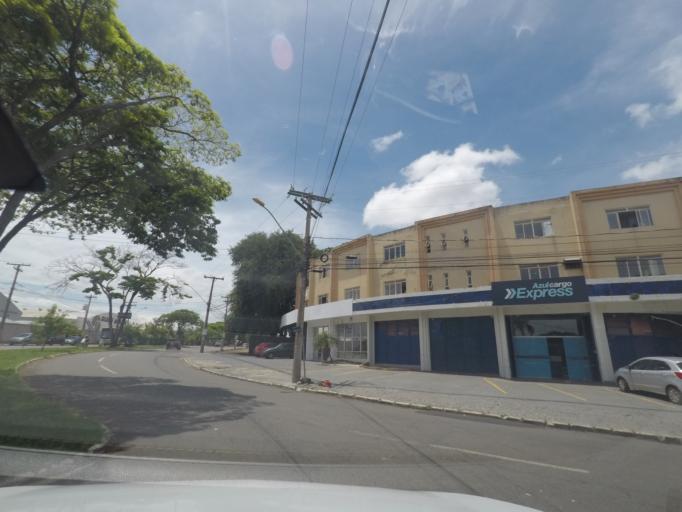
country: BR
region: Goias
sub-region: Goiania
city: Goiania
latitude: -16.6314
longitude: -49.2314
